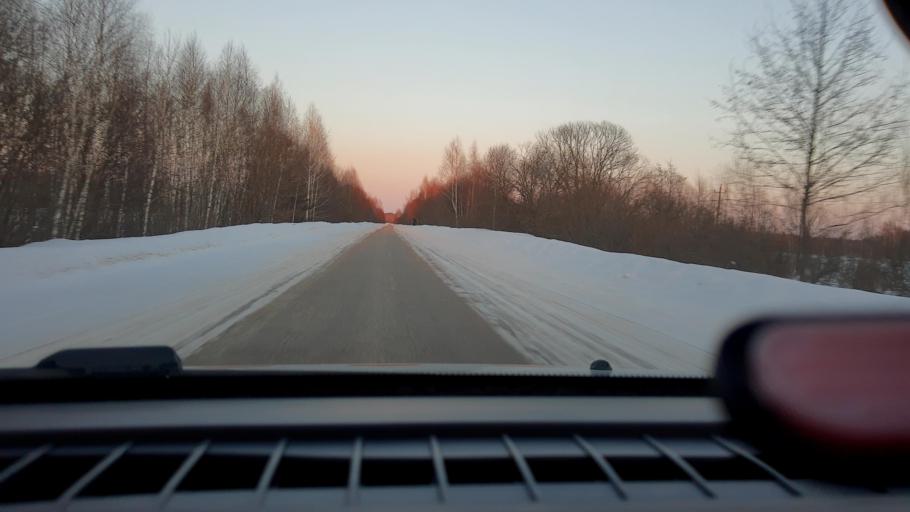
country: RU
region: Nizjnij Novgorod
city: Lyskovo
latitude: 56.1613
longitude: 45.1800
